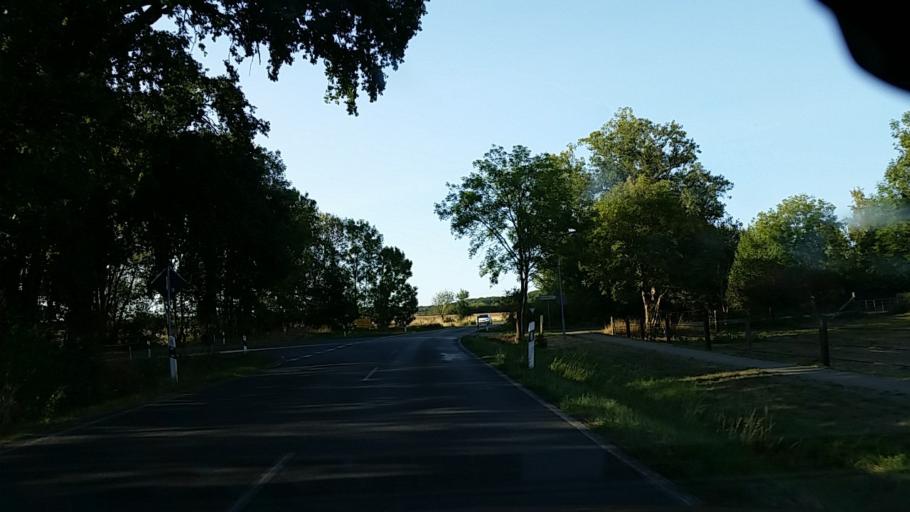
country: DE
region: Lower Saxony
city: Lehre
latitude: 52.3222
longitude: 10.6333
